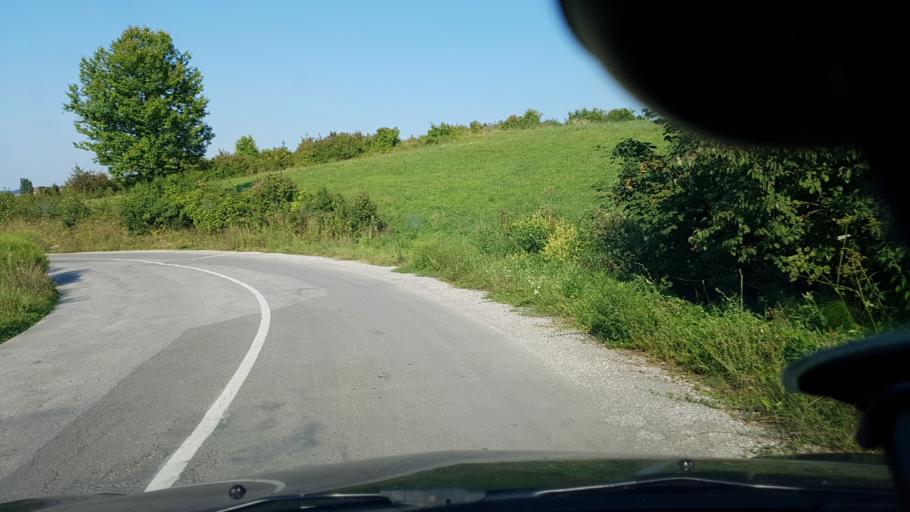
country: HR
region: Zagrebacka
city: Bregana
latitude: 45.9066
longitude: 15.6884
